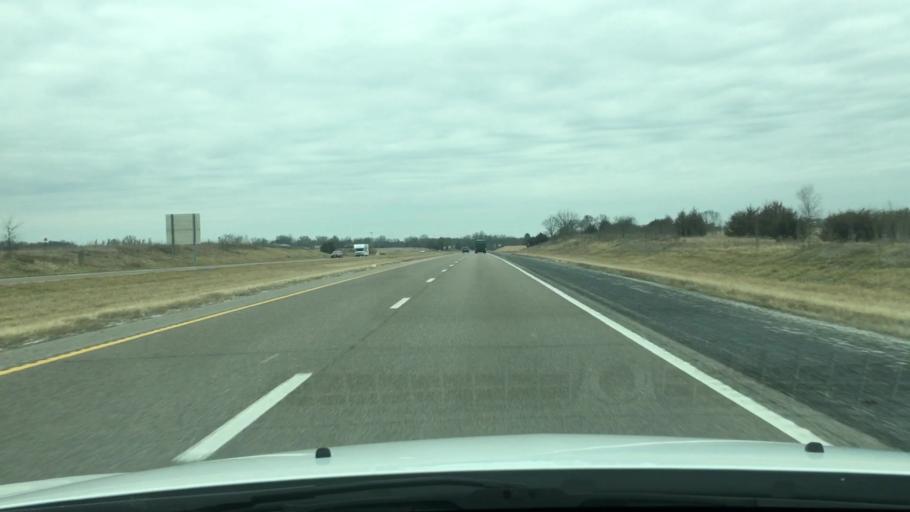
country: US
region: Missouri
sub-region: Audrain County
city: Mexico
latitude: 39.0343
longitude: -91.8887
